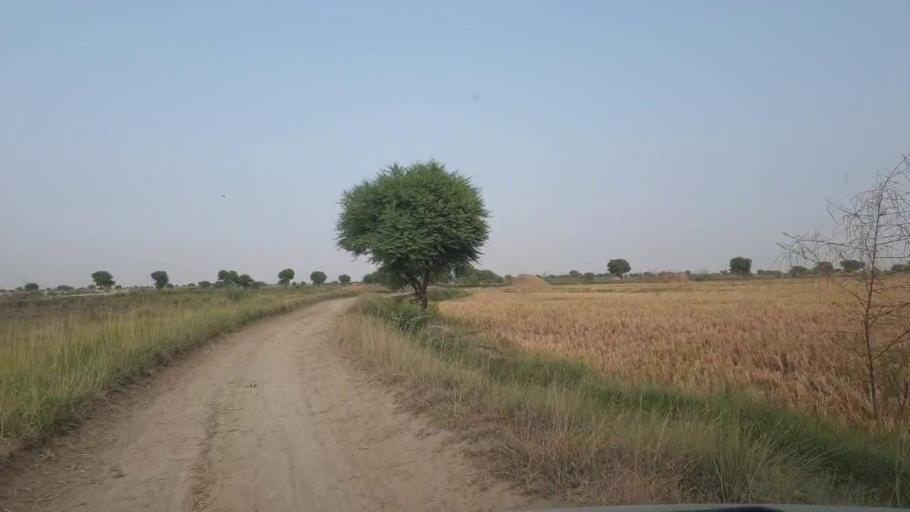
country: PK
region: Sindh
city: Matli
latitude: 25.0413
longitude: 68.7449
